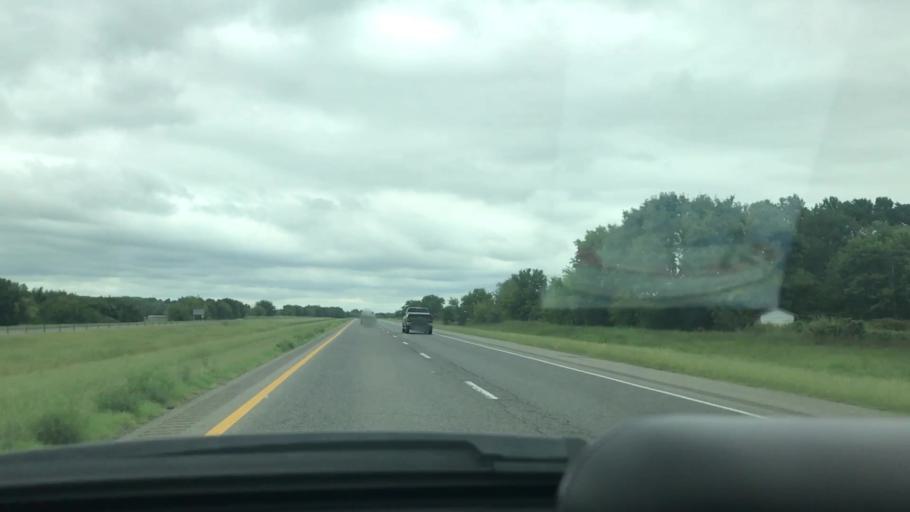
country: US
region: Oklahoma
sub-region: McIntosh County
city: Checotah
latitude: 35.4204
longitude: -95.5558
